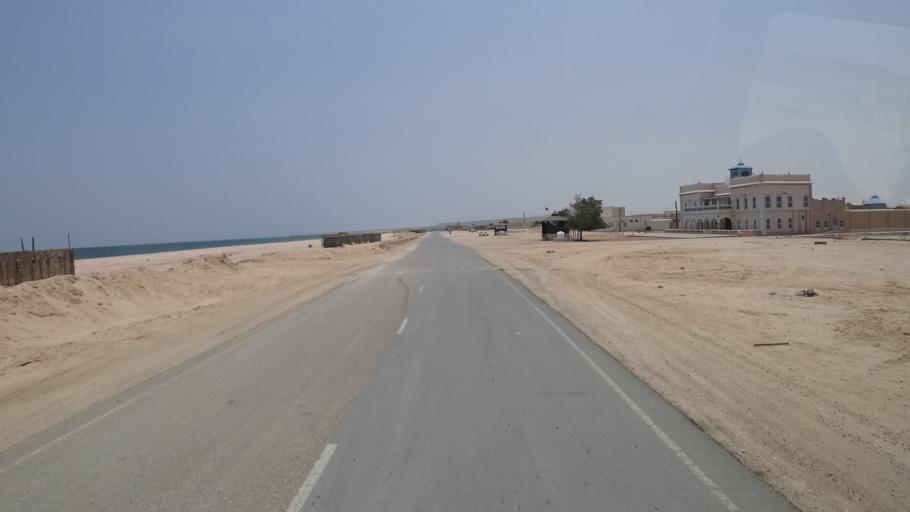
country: OM
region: Ash Sharqiyah
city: Sur
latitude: 22.5259
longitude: 59.7976
